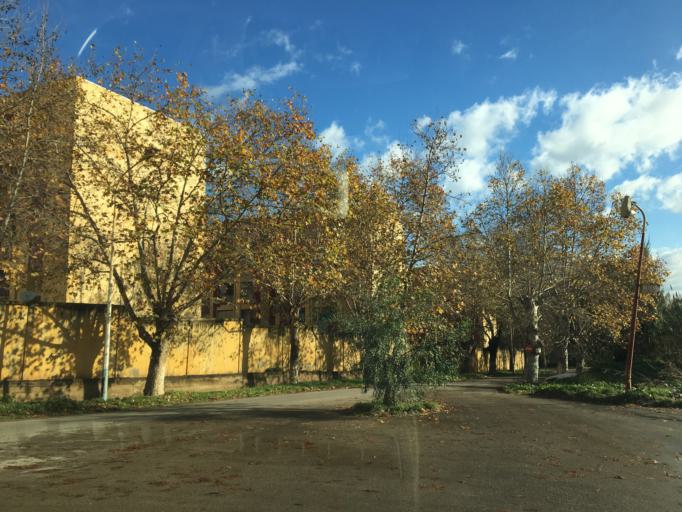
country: DZ
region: Tipaza
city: Tipasa
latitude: 36.5687
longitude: 2.3958
